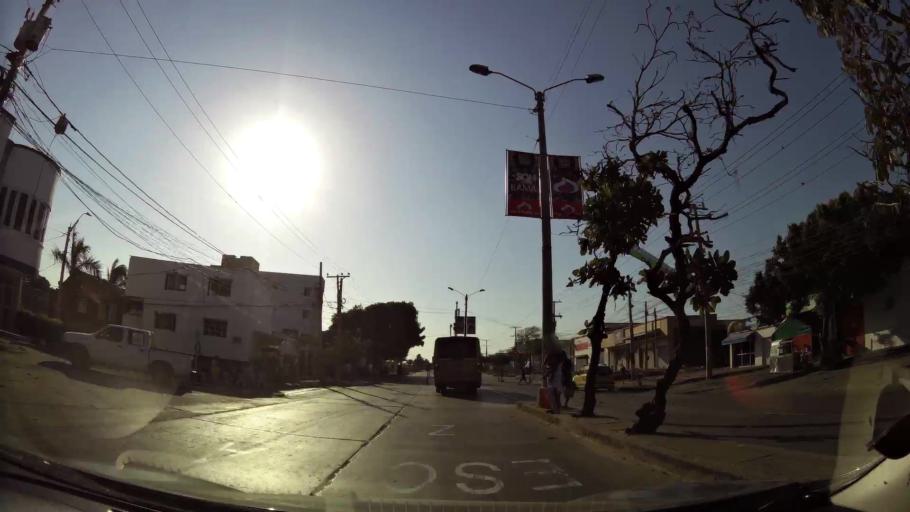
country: CO
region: Atlantico
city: Barranquilla
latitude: 11.0253
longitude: -74.8028
